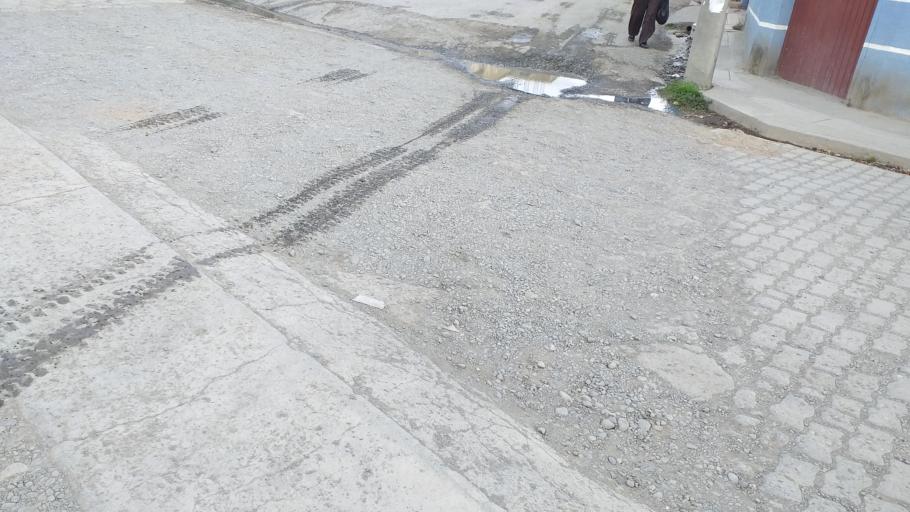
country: BO
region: La Paz
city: Achacachi
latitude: -16.0434
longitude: -68.6885
